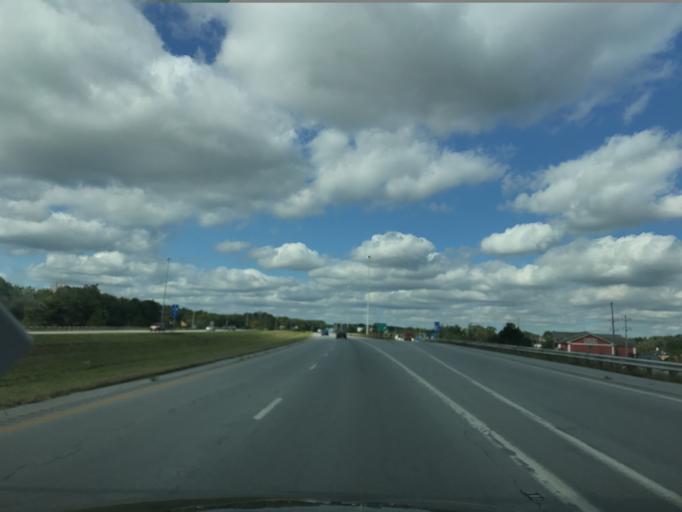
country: US
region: Ohio
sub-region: Summit County
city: Twinsburg
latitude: 41.3044
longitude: -81.4353
